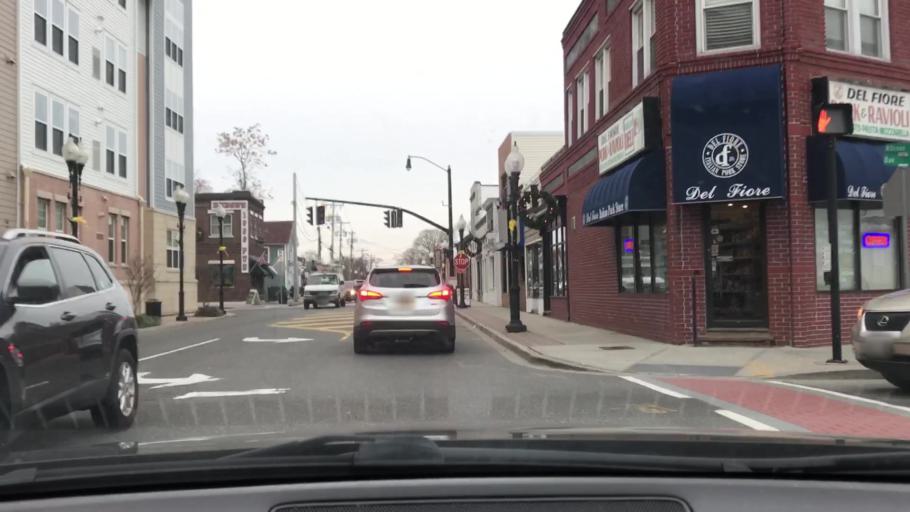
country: US
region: New York
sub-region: Suffolk County
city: Patchogue
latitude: 40.7665
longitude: -73.0151
